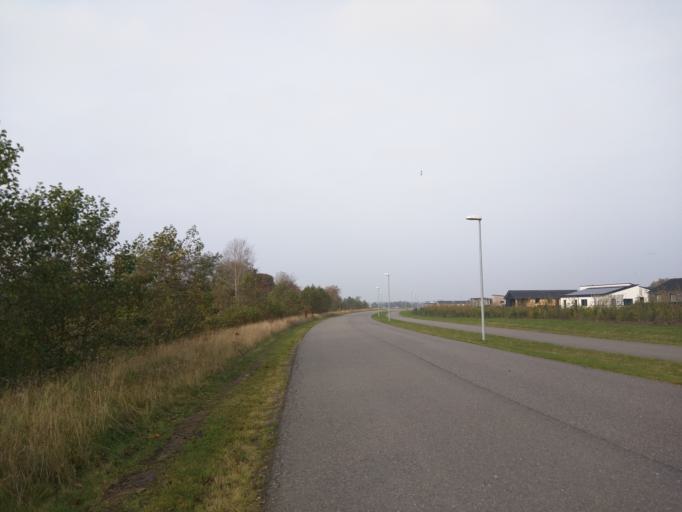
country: DK
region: Central Jutland
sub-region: Viborg Kommune
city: Viborg
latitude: 56.4404
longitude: 9.3563
